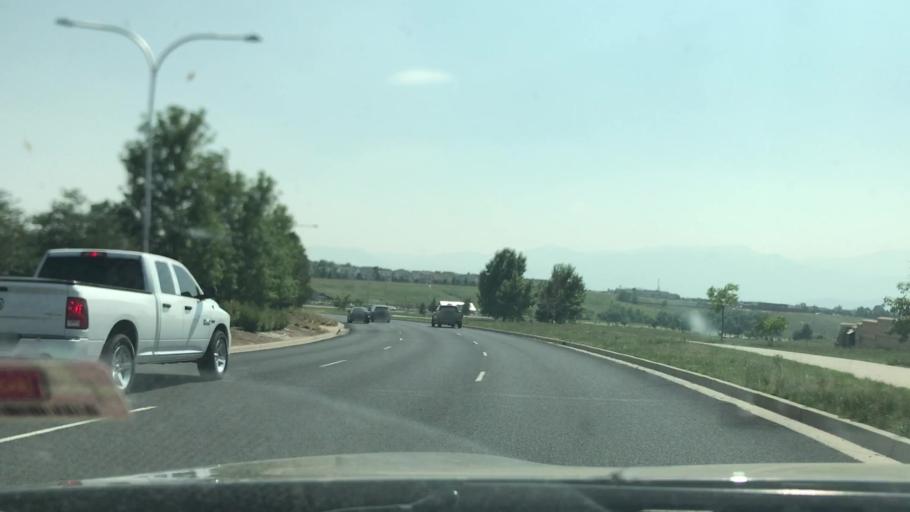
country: US
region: Colorado
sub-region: El Paso County
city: Black Forest
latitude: 38.9684
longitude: -104.7572
